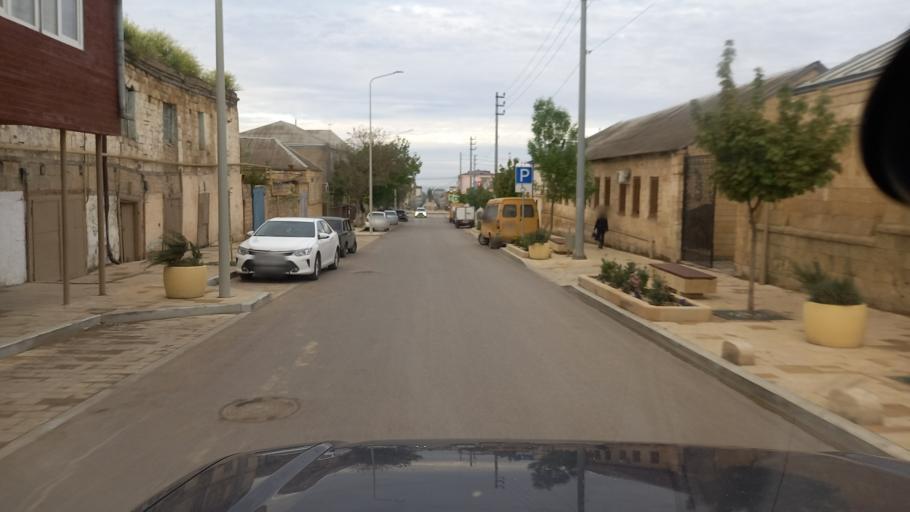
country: RU
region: Dagestan
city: Derbent
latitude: 42.0574
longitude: 48.2866
